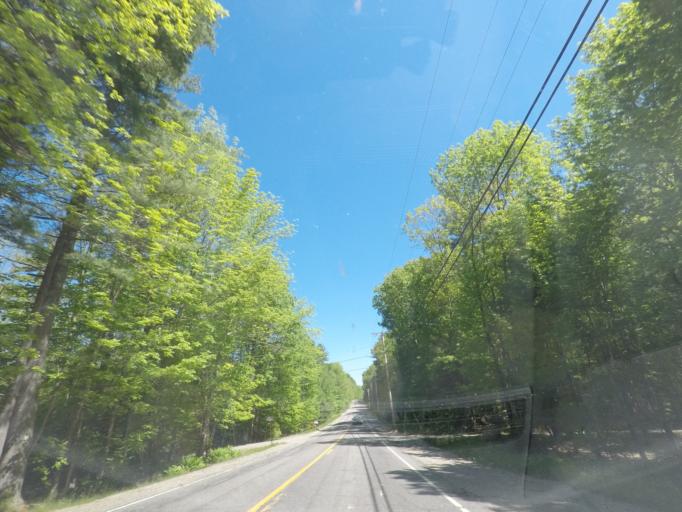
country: US
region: Maine
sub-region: Kennebec County
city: Manchester
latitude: 44.2877
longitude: -69.8892
